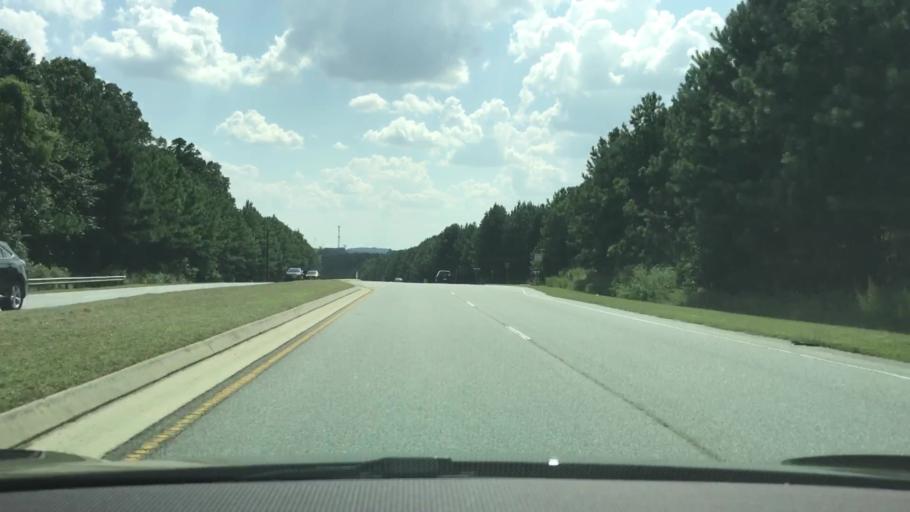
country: US
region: Georgia
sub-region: Gwinnett County
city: Sugar Hill
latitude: 34.0591
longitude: -84.0221
